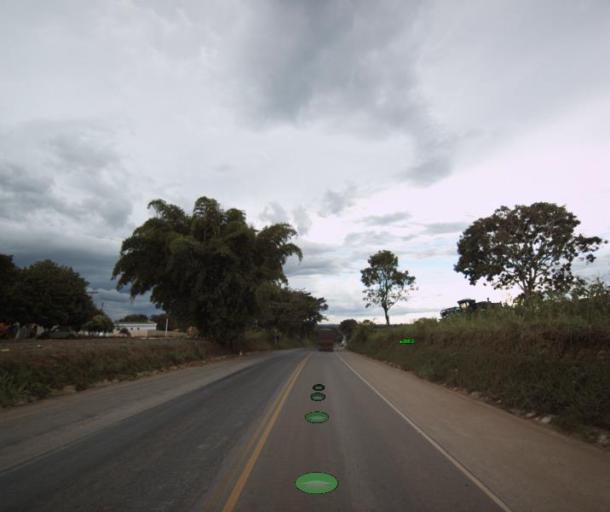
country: BR
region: Goias
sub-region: Itapaci
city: Itapaci
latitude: -15.0373
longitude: -49.4374
